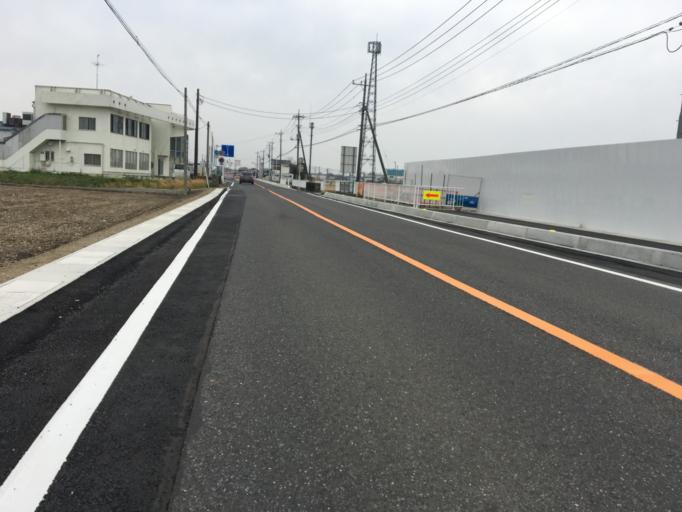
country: JP
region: Saitama
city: Kazo
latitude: 36.1172
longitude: 139.5961
